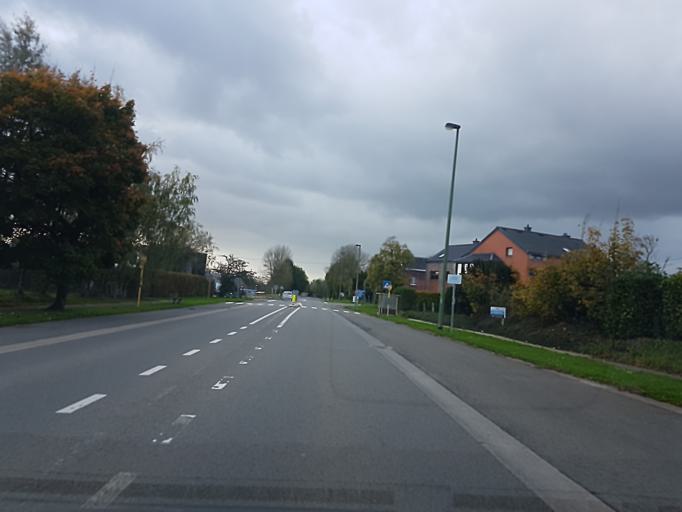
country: BE
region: Wallonia
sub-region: Province de Liege
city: Olne
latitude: 50.5393
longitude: 5.7432
